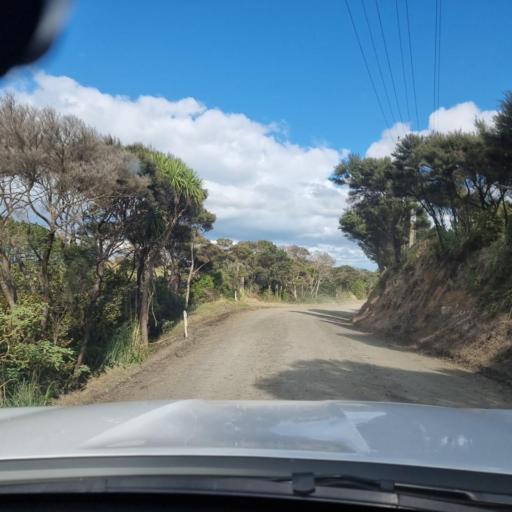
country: NZ
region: Auckland
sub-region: Auckland
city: Wellsford
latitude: -36.3170
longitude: 174.1347
